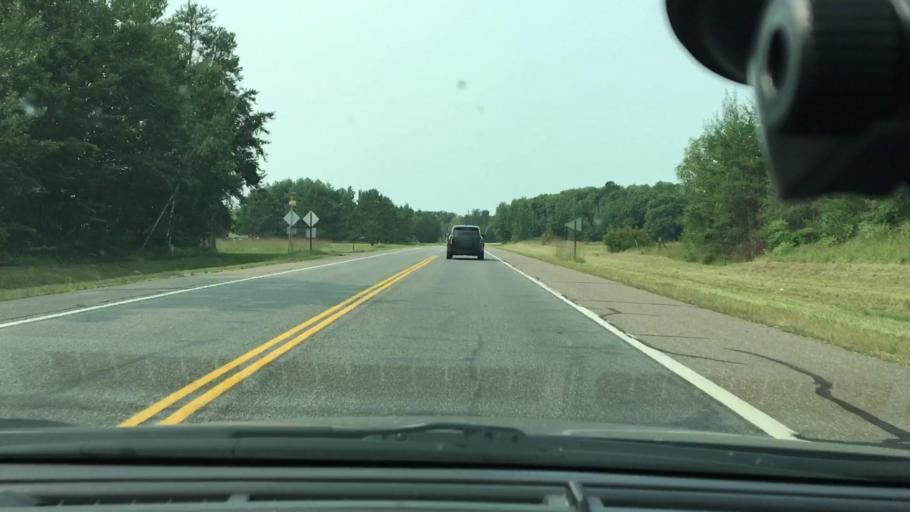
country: US
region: Minnesota
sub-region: Crow Wing County
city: Breezy Point
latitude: 46.4848
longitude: -94.1616
